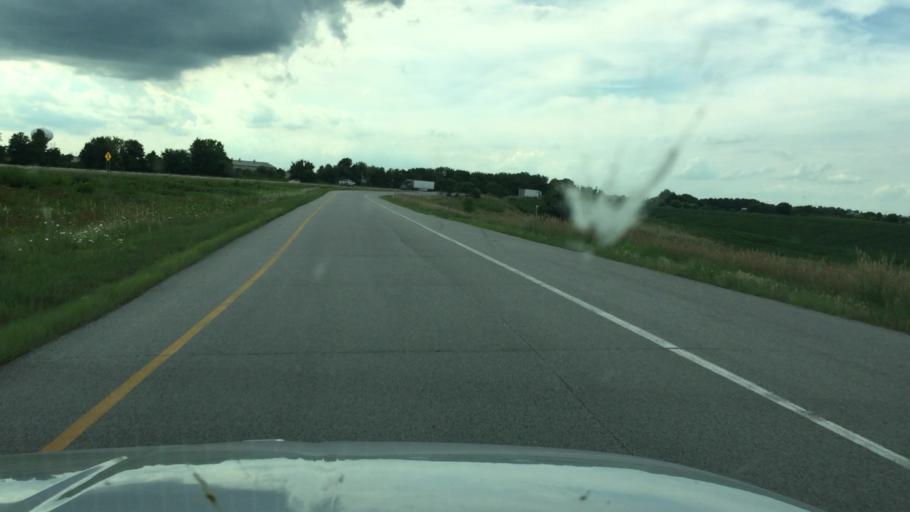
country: US
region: Iowa
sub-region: Scott County
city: Blue Grass
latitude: 41.5396
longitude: -90.6754
